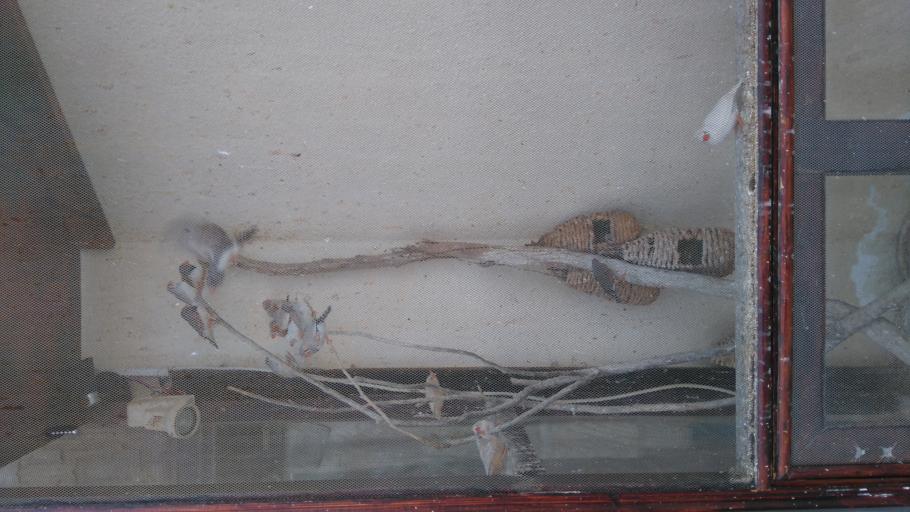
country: EG
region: Red Sea
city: Makadi Bay
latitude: 27.0813
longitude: 33.8682
